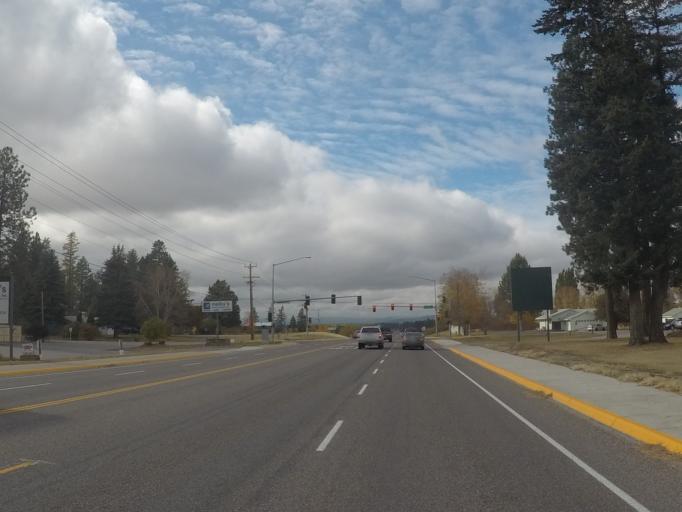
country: US
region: Montana
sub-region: Flathead County
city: Columbia Falls
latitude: 48.3707
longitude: -114.2178
